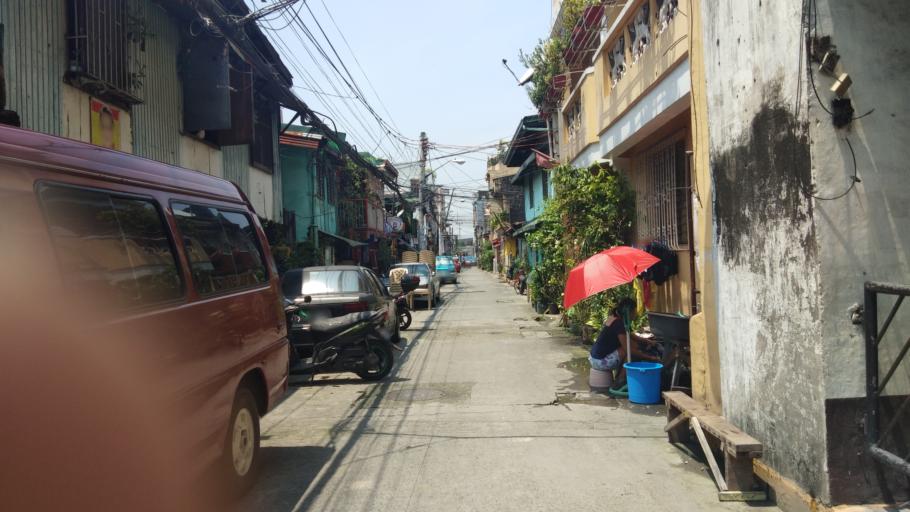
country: PH
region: Metro Manila
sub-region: San Juan
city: San Juan
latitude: 14.5869
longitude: 121.0128
